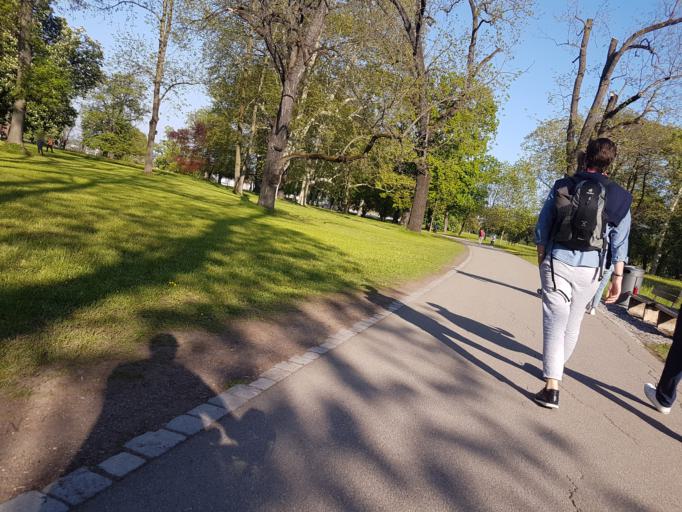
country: DE
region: Baden-Wuerttemberg
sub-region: Regierungsbezirk Stuttgart
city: Stuttgart-Ost
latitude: 48.8008
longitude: 9.2014
